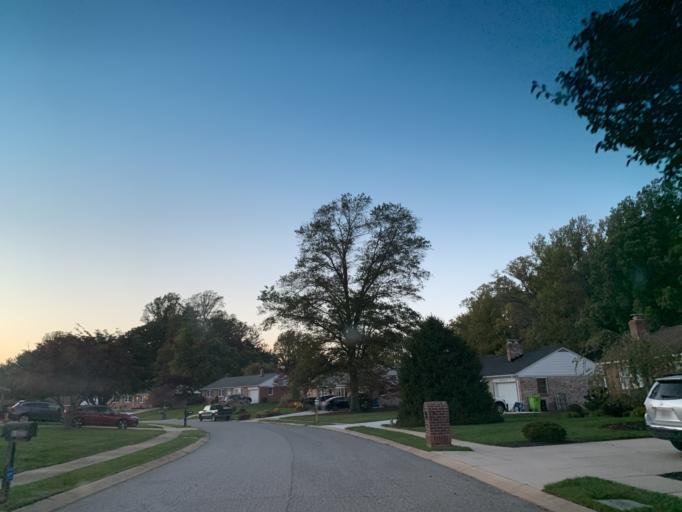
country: US
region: Maryland
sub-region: Harford County
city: South Bel Air
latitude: 39.5471
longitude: -76.3025
